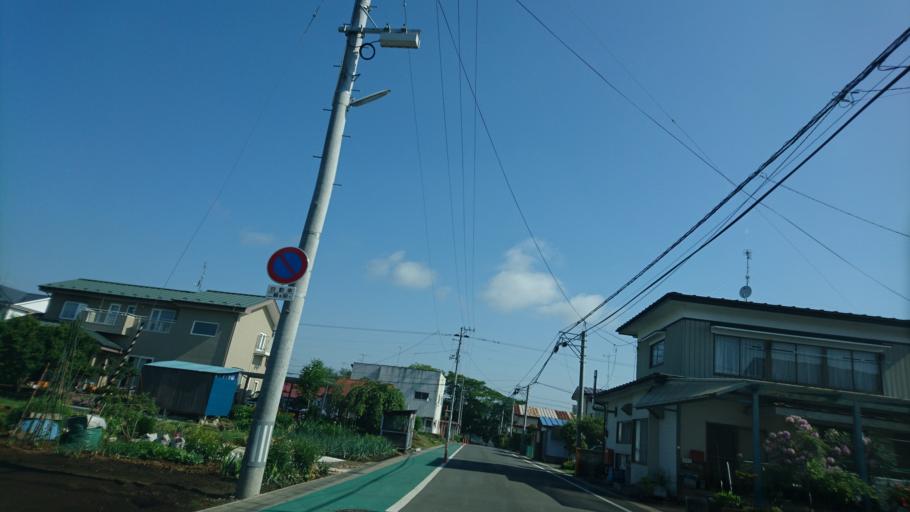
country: JP
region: Iwate
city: Ichinoseki
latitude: 38.9262
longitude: 141.1101
